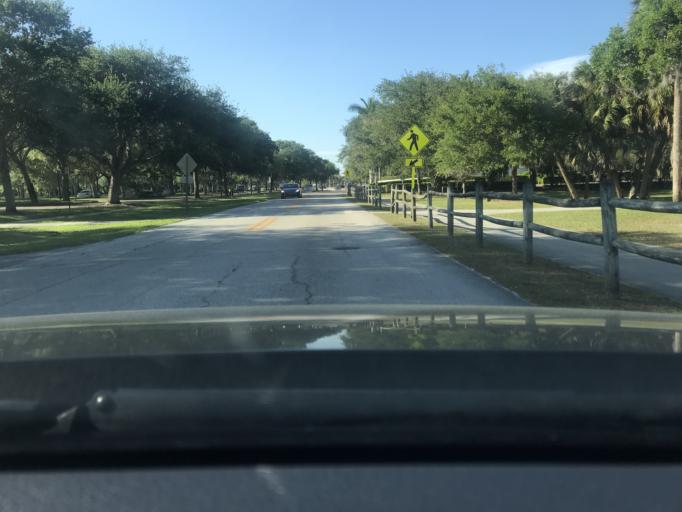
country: US
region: Florida
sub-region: Indian River County
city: Vero Beach
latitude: 27.6508
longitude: -80.3665
